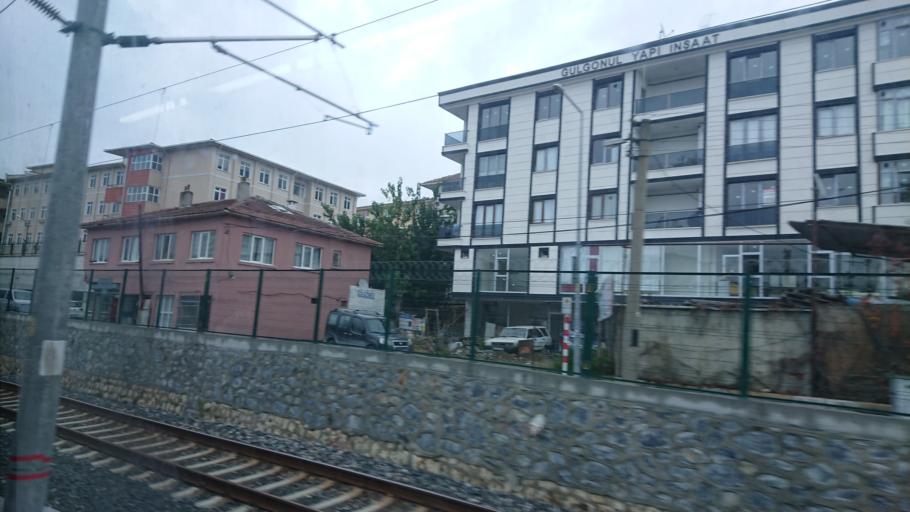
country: TR
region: Istanbul
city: Mahmutbey
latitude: 40.9905
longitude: 28.7726
